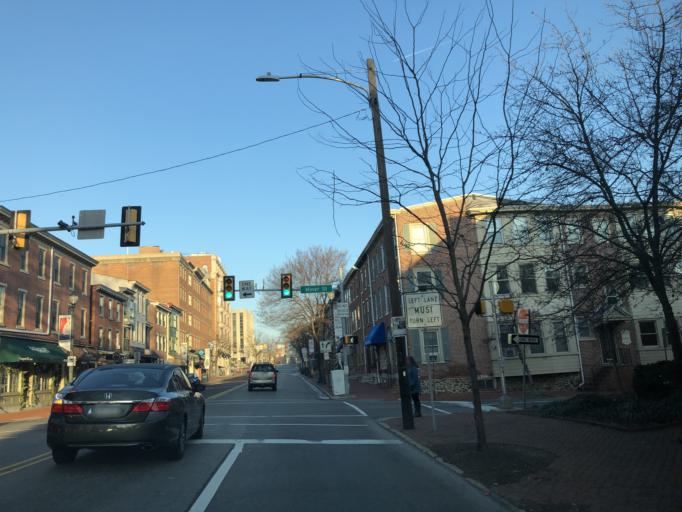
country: US
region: Pennsylvania
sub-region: Chester County
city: West Chester
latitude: 39.9586
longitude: -75.6033
